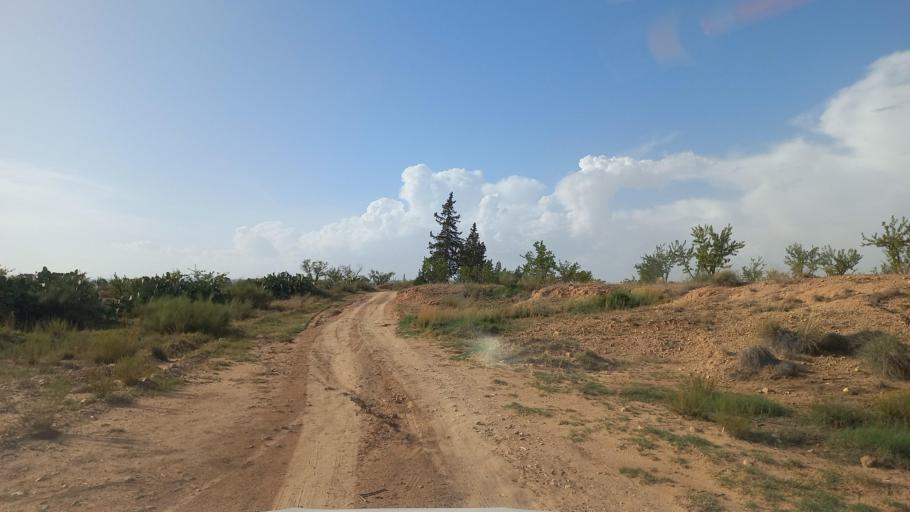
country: TN
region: Al Qasrayn
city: Kasserine
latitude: 35.2288
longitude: 8.9677
